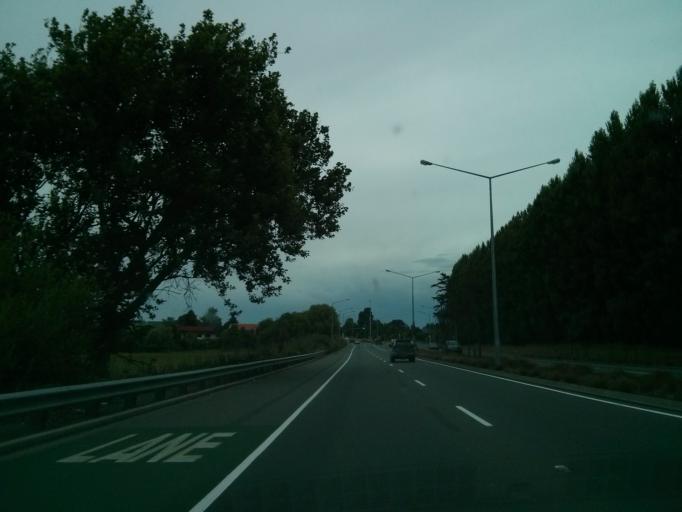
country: NZ
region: Canterbury
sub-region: Christchurch City
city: Christchurch
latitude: -43.4649
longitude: 172.6195
